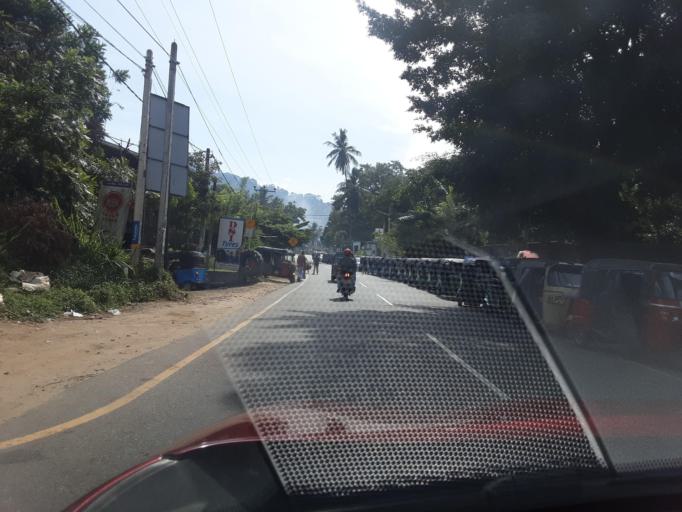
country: LK
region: Uva
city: Badulla
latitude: 6.9841
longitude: 81.0678
